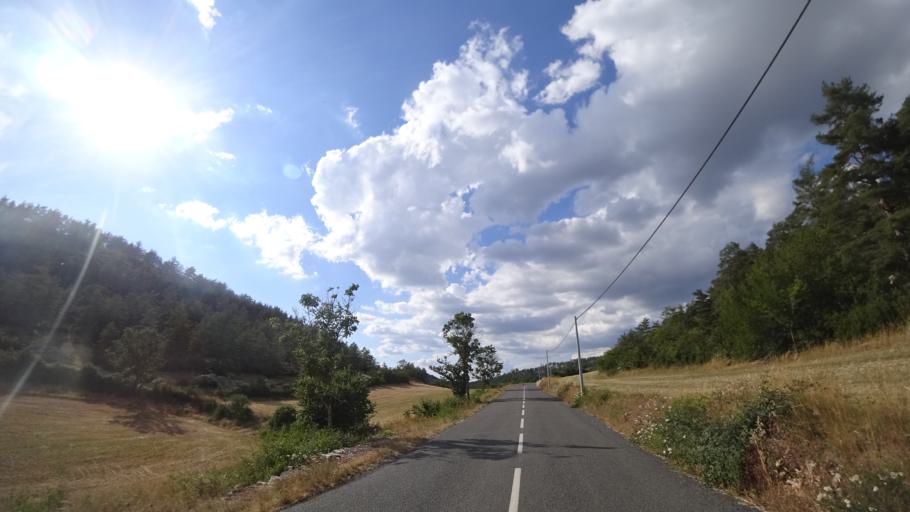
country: FR
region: Languedoc-Roussillon
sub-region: Departement de la Lozere
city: Chanac
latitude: 44.3638
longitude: 3.3525
